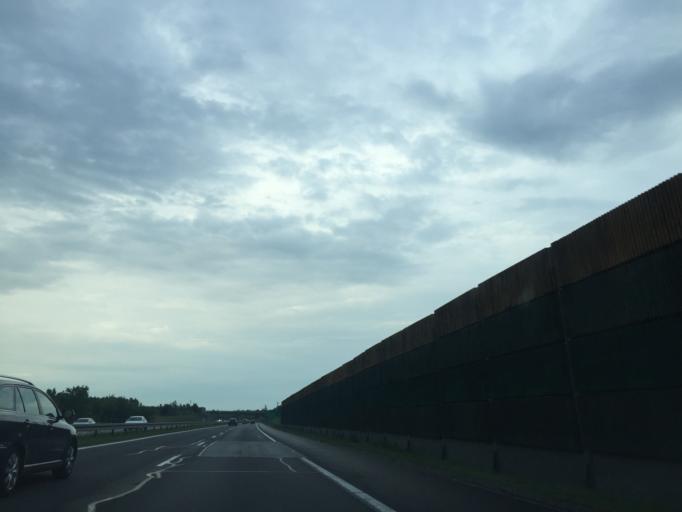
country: PL
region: Masovian Voivodeship
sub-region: Powiat ostrowski
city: Ostrow Mazowiecka
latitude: 52.8025
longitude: 21.8719
